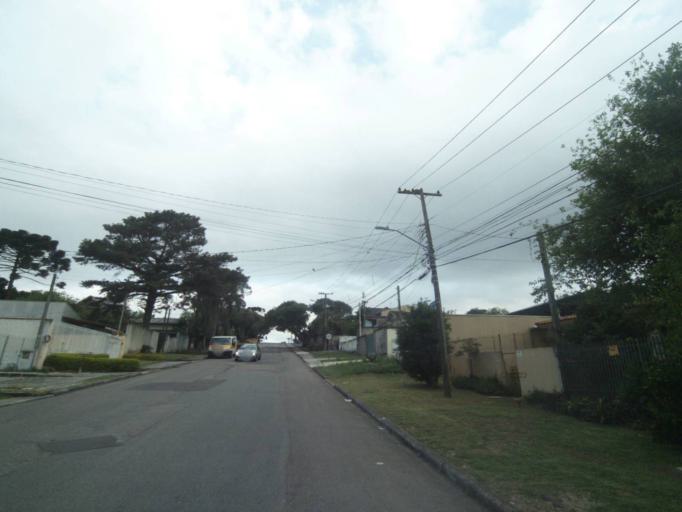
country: BR
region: Parana
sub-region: Pinhais
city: Pinhais
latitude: -25.4132
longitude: -49.2163
